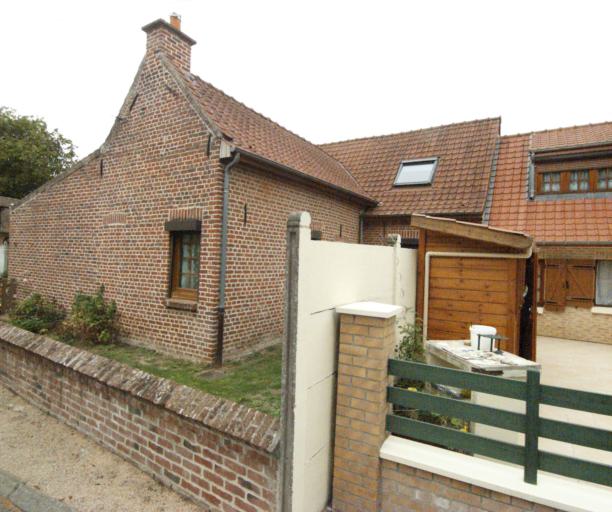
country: FR
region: Nord-Pas-de-Calais
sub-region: Departement du Nord
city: Fretin
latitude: 50.5555
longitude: 3.1509
